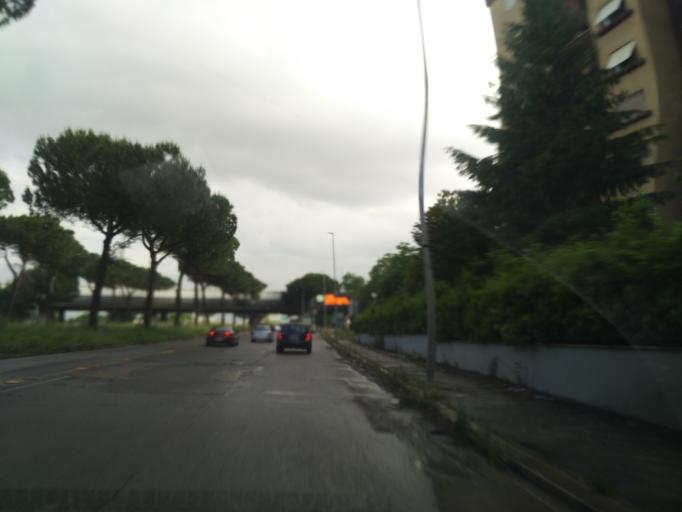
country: IT
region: Latium
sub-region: Citta metropolitana di Roma Capitale
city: Rome
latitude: 41.9091
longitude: 12.5724
